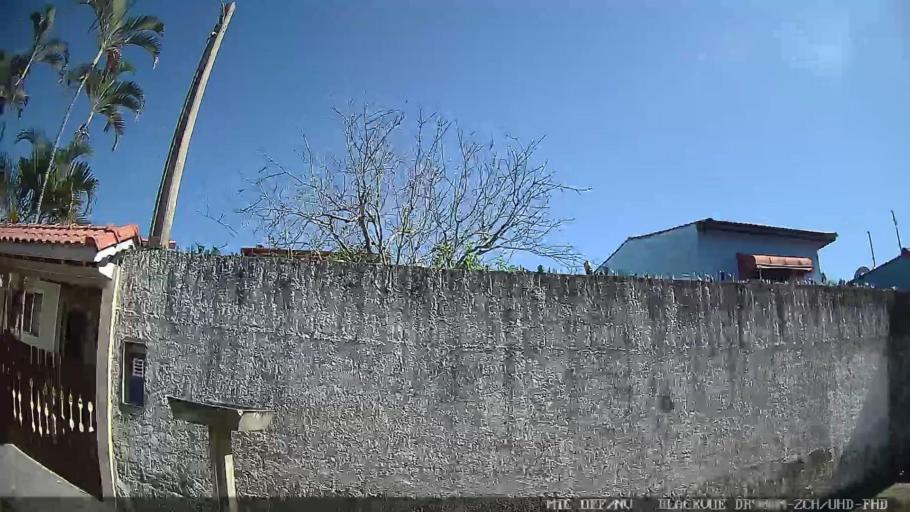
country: BR
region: Sao Paulo
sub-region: Peruibe
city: Peruibe
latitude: -24.2769
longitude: -46.9398
